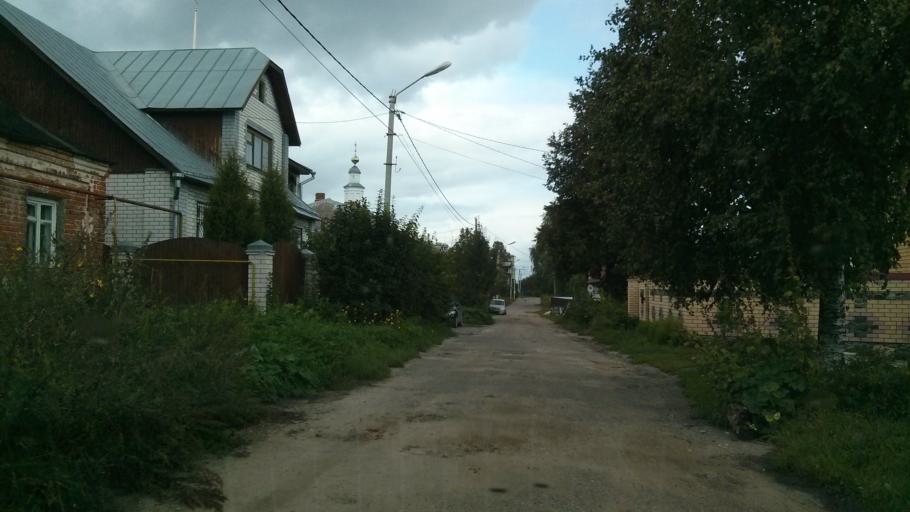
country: RU
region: Vladimir
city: Murom
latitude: 55.5752
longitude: 42.0652
